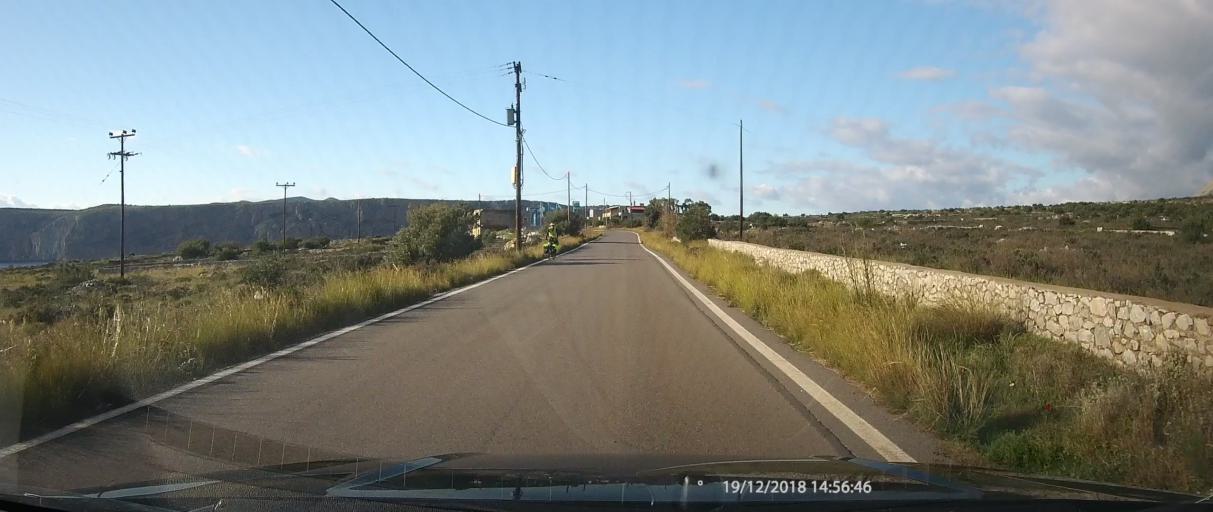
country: GR
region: Peloponnese
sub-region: Nomos Lakonias
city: Gytheio
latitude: 36.4781
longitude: 22.4132
